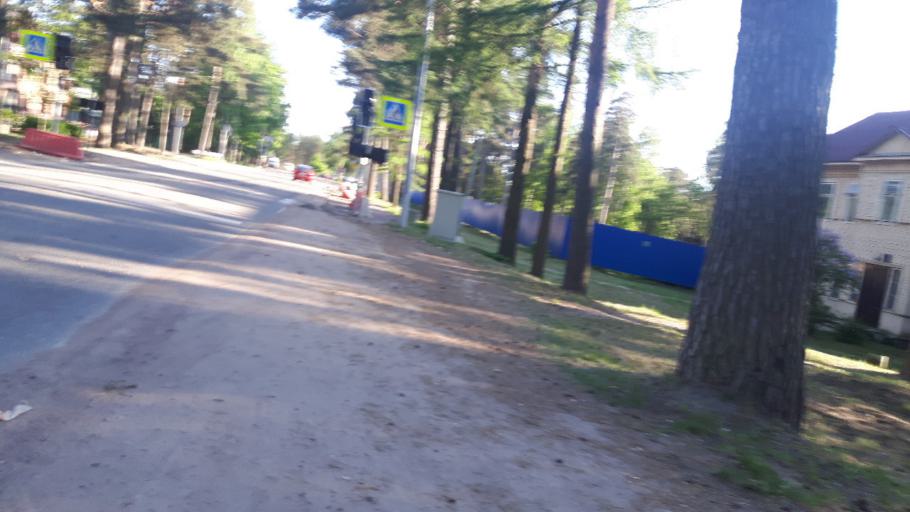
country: RU
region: Leningrad
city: Vistino
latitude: 59.7714
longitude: 28.4745
